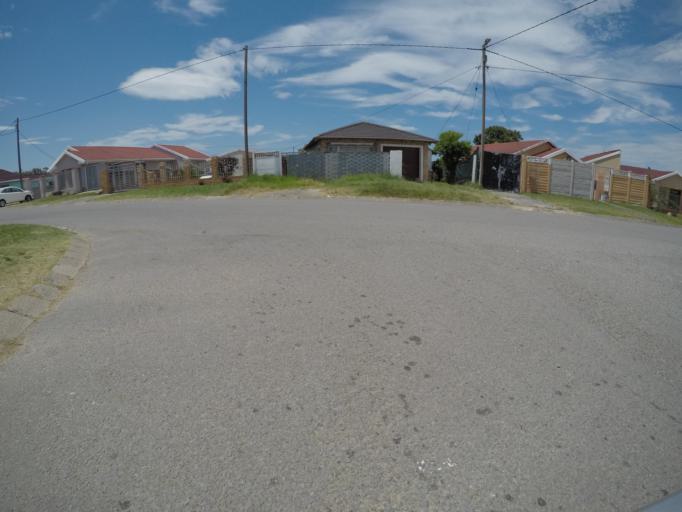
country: ZA
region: Eastern Cape
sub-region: Buffalo City Metropolitan Municipality
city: East London
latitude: -33.0478
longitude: 27.8499
